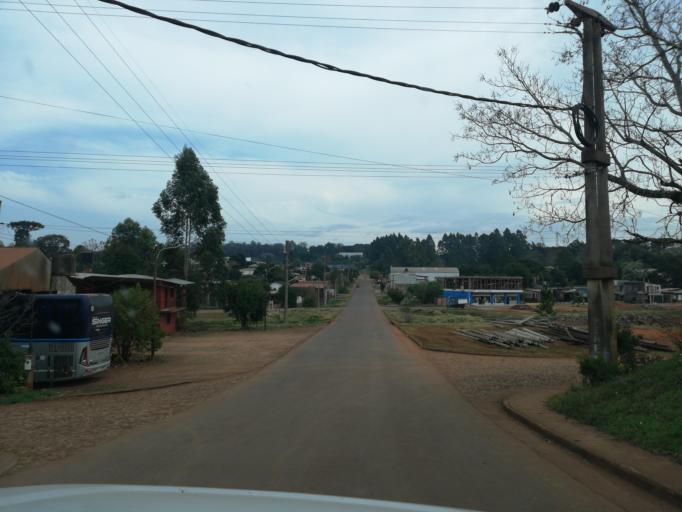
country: AR
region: Misiones
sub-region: Departamento de San Pedro
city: San Pedro
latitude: -26.6255
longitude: -54.1102
